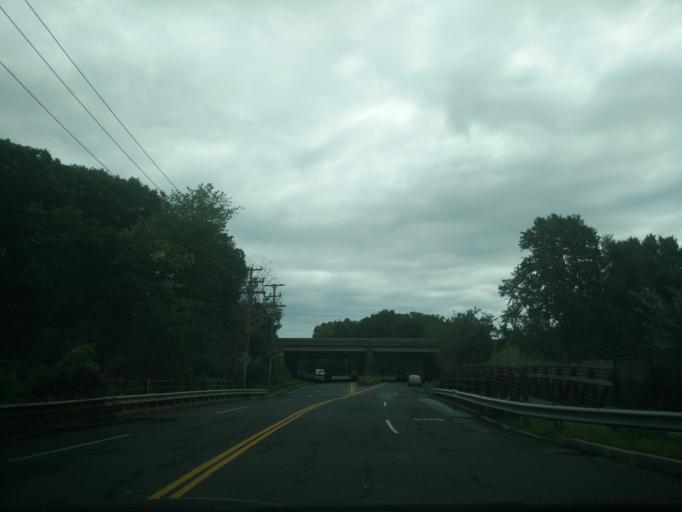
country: US
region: Connecticut
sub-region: New Haven County
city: Milford
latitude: 41.2356
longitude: -73.0310
